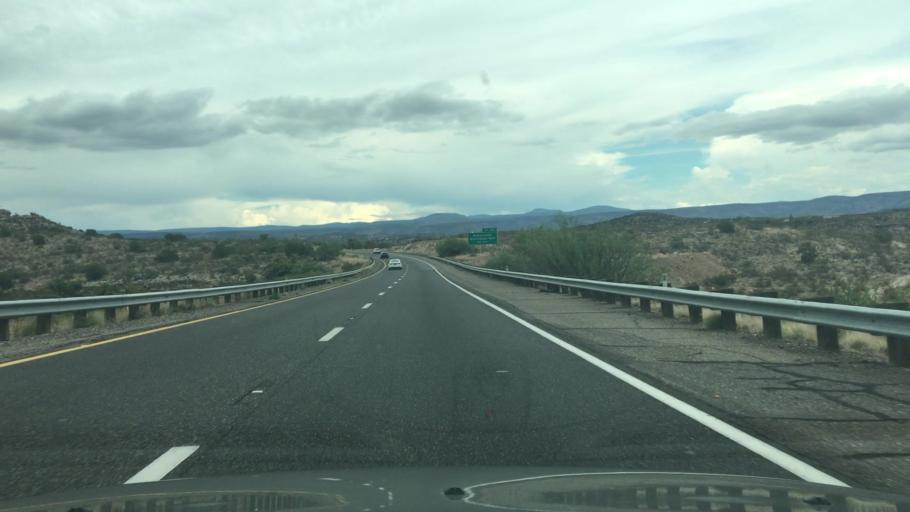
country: US
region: Arizona
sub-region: Yavapai County
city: Lake Montezuma
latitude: 34.6248
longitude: -111.8392
